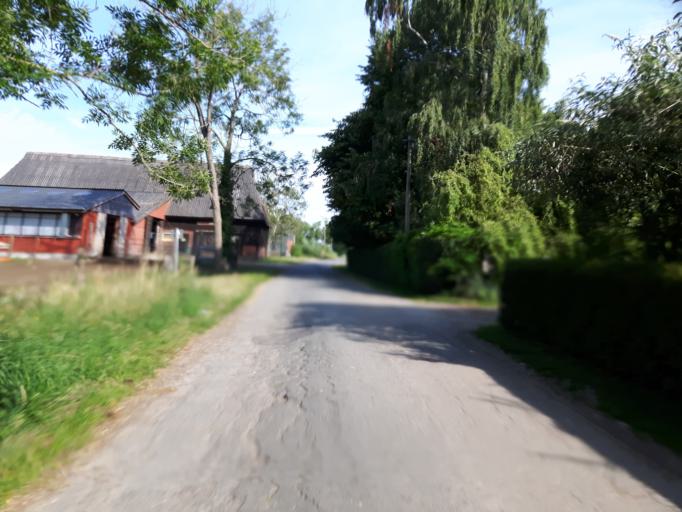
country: DE
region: Lower Saxony
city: Neuenkirchen
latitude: 53.1733
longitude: 8.5081
